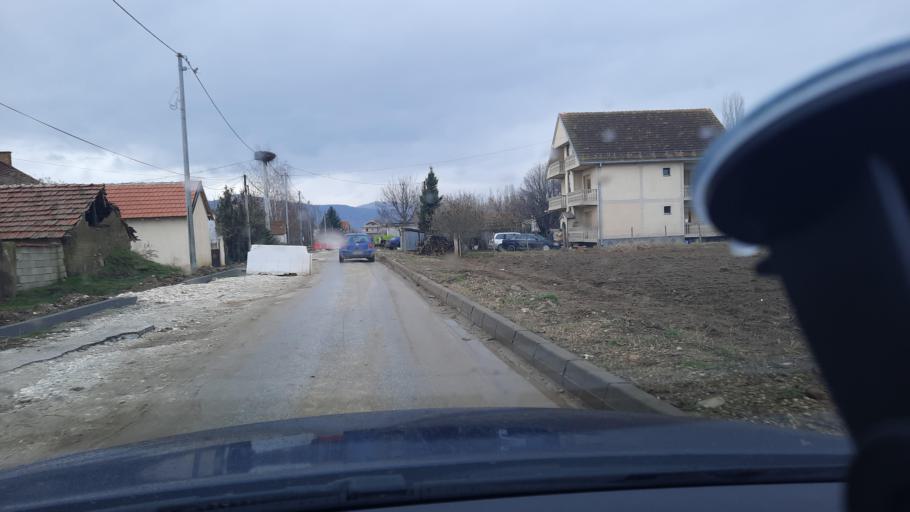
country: MK
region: Mogila
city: Mogila
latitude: 41.1100
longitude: 21.3868
